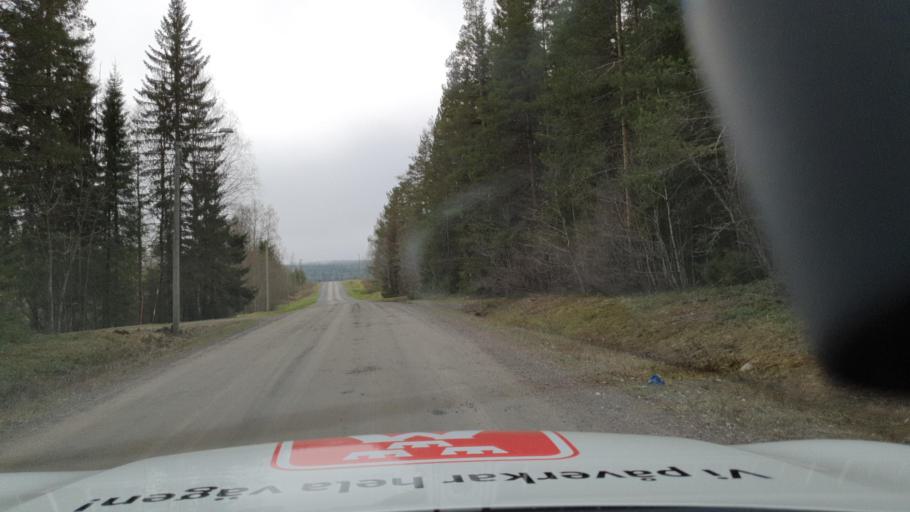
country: SE
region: Vaesterbotten
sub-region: Bjurholms Kommun
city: Bjurholm
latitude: 63.7952
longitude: 19.3323
